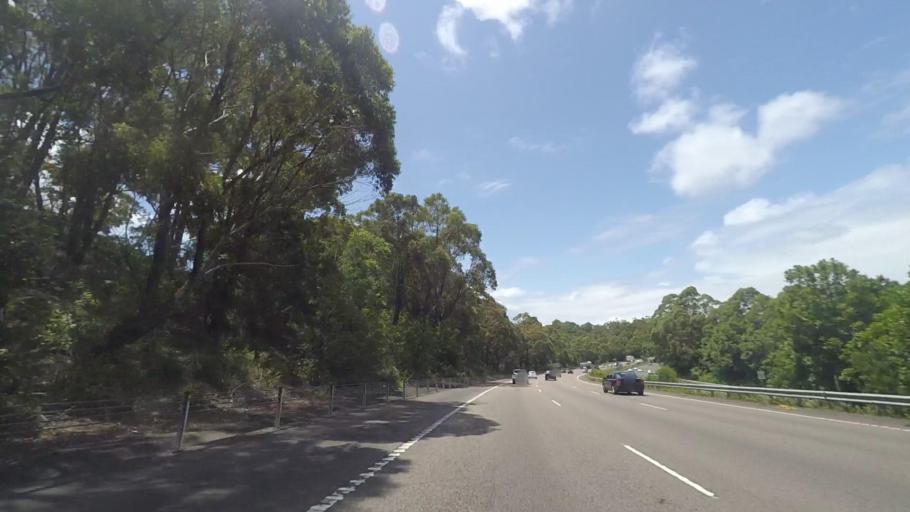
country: AU
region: New South Wales
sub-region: Gosford Shire
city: Lisarow
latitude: -33.3625
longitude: 151.3338
